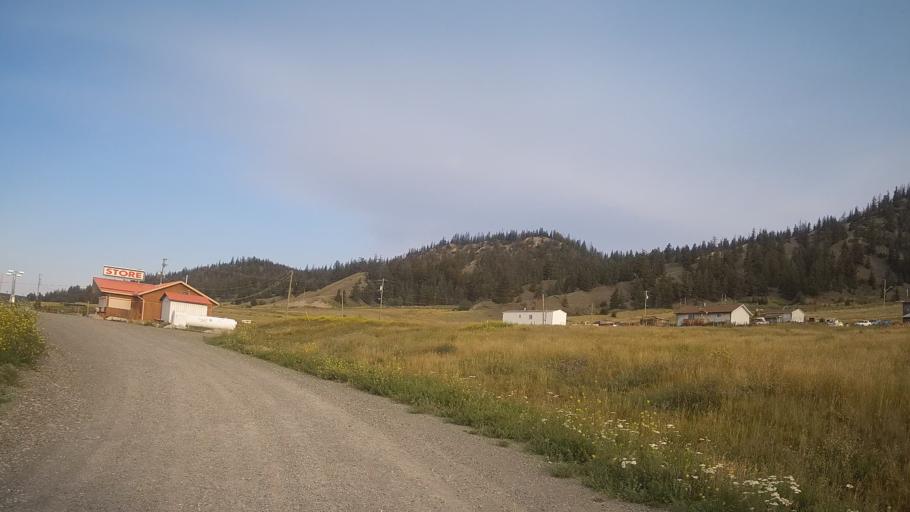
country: CA
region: British Columbia
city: Hanceville
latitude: 52.1409
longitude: -123.9514
